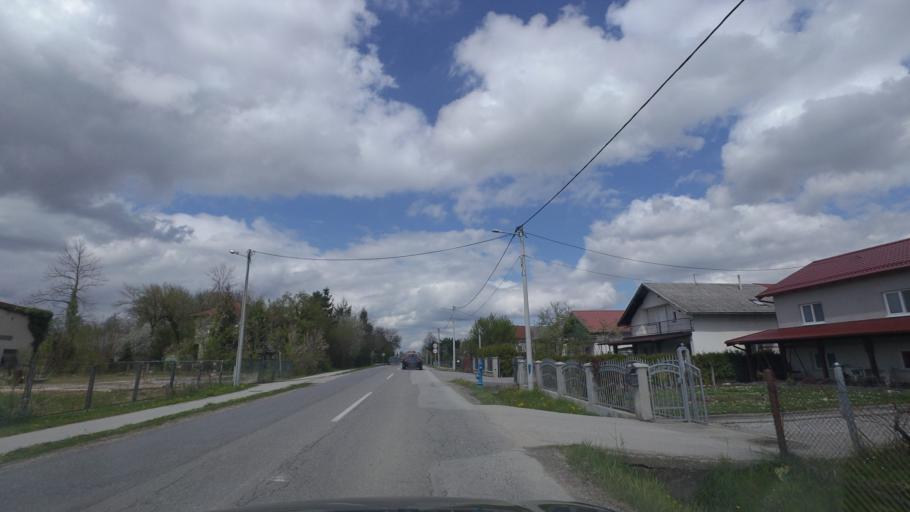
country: HR
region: Zagrebacka
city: Kerestinec
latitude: 45.7603
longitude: 15.8068
